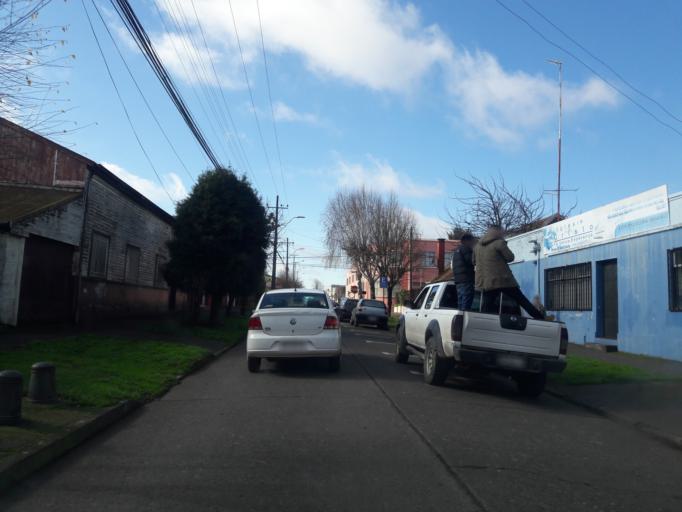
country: CL
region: Araucania
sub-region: Provincia de Malleco
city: Victoria
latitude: -38.2325
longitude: -72.3343
